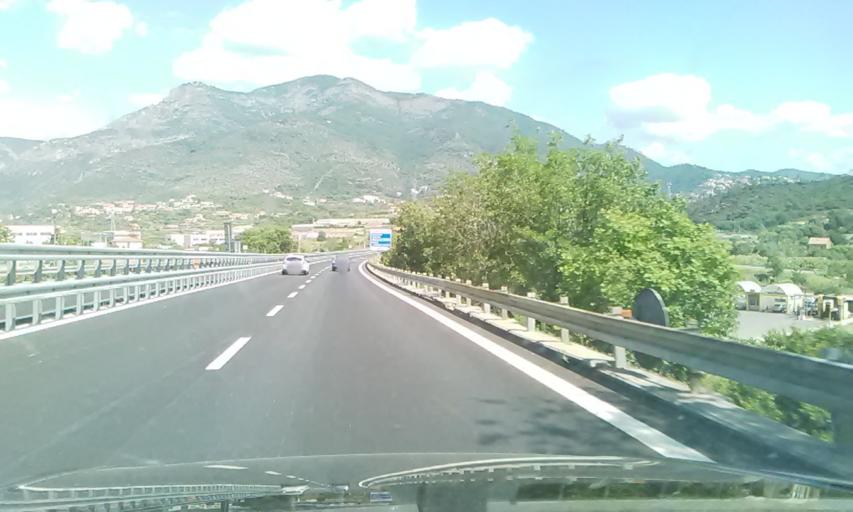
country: IT
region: Liguria
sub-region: Provincia di Savona
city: Borghetto Santo Spirito
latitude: 44.1174
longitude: 8.2267
